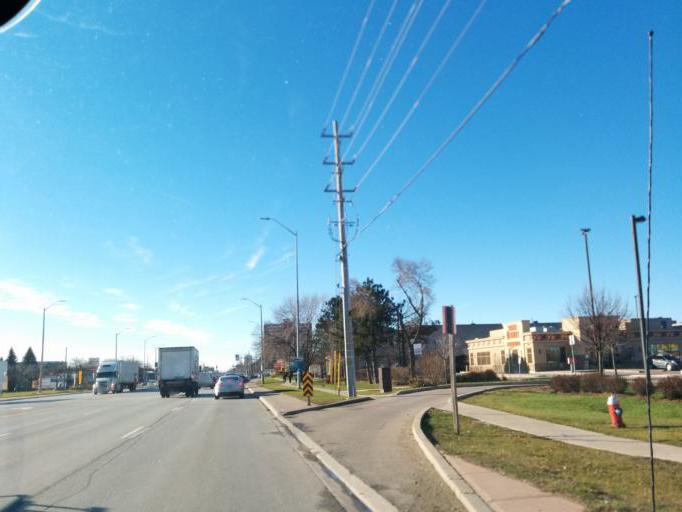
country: CA
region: Ontario
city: Etobicoke
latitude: 43.6113
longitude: -79.5818
